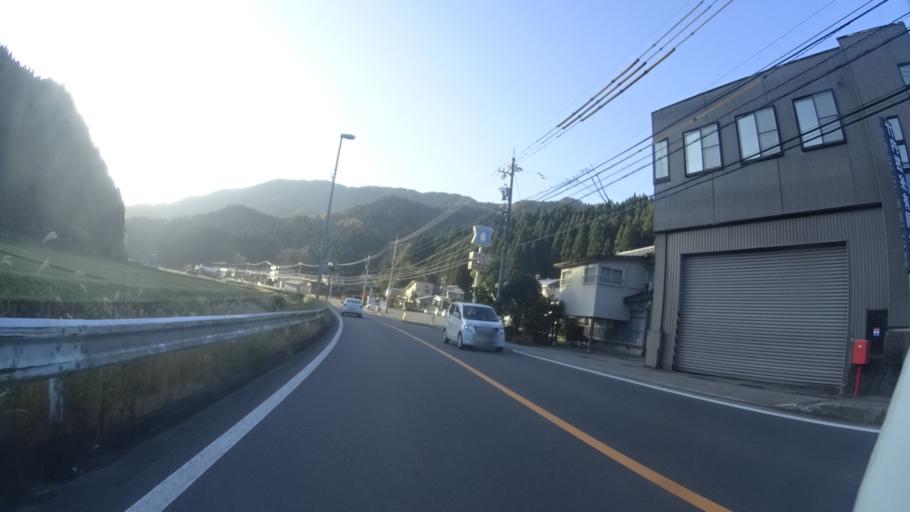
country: JP
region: Fukui
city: Ono
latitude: 36.0090
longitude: 136.3926
